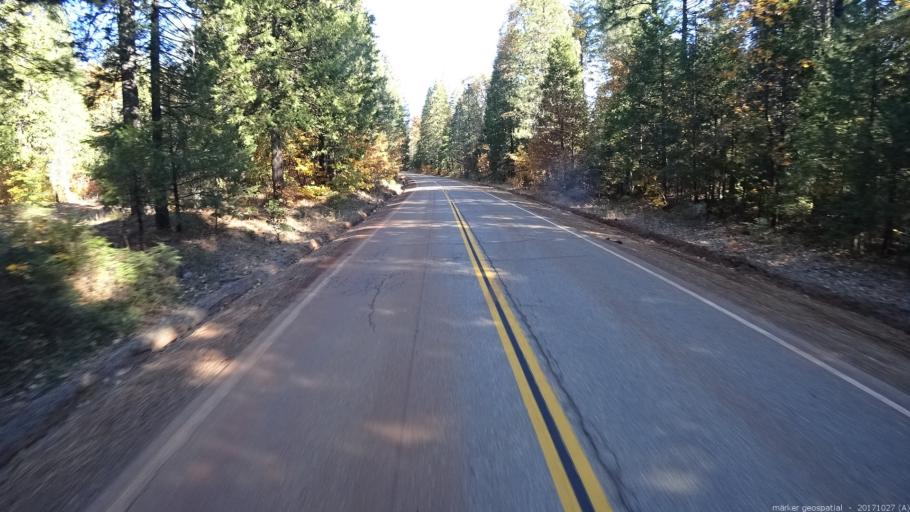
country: US
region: California
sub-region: Shasta County
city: Burney
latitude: 40.9462
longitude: -121.9477
